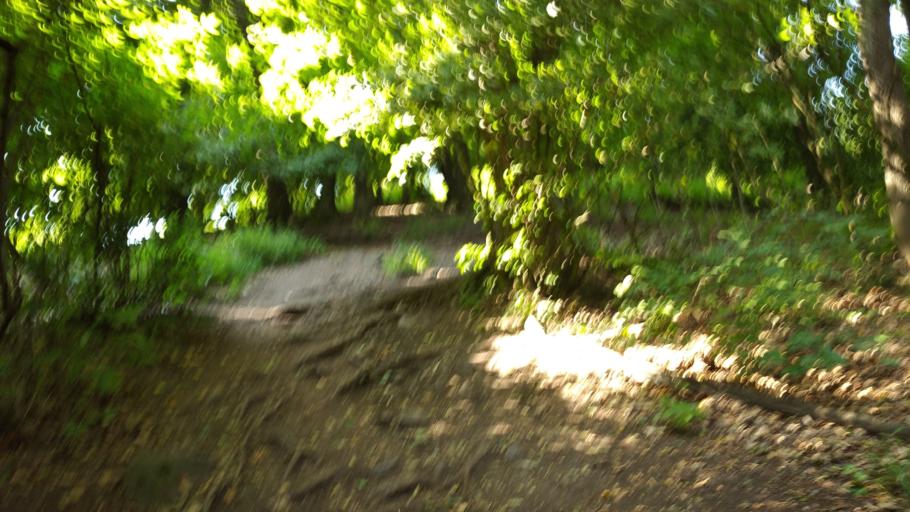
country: HU
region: Pest
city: Nagymaros
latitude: 47.7846
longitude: 18.9339
